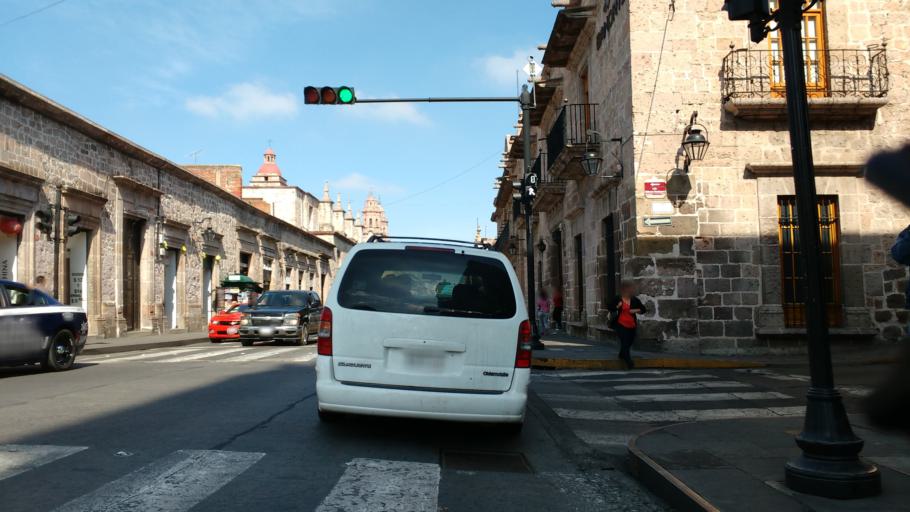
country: MX
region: Michoacan
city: Morelia
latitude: 19.7029
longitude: -101.1887
